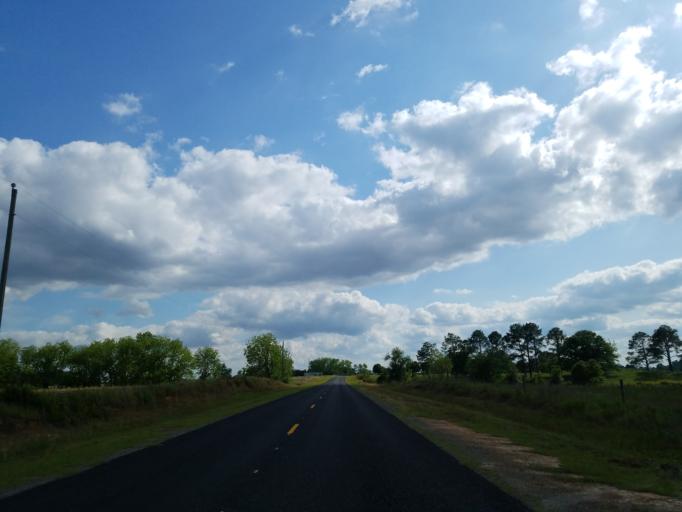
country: US
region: Georgia
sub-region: Dooly County
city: Unadilla
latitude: 32.2195
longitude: -83.7700
